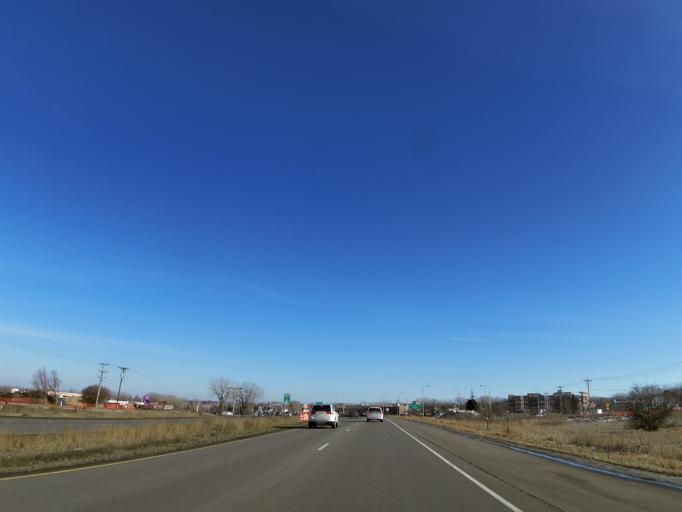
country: US
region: Minnesota
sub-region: Dakota County
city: Burnsville
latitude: 44.7762
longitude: -93.2815
